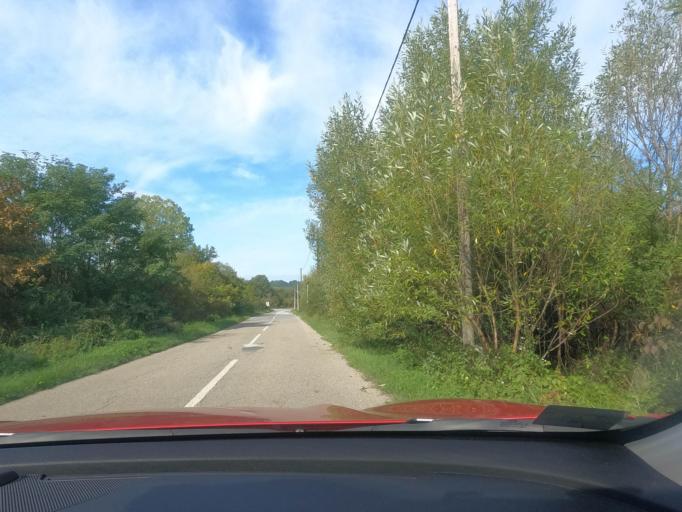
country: HR
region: Sisacko-Moslavacka
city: Glina
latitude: 45.2998
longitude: 16.1342
